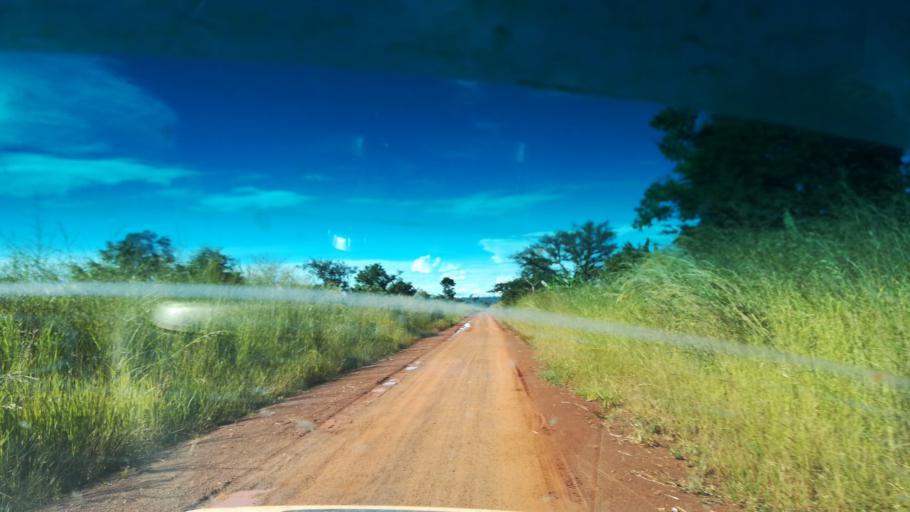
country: ZM
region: Luapula
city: Nchelenge
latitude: -9.3678
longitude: 28.2161
